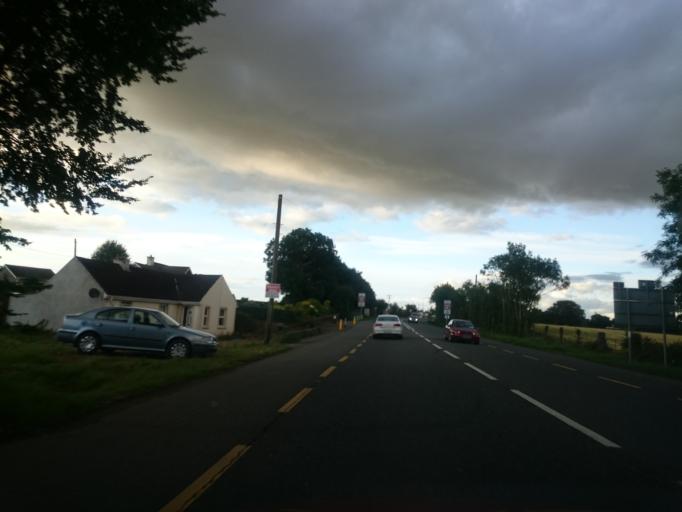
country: IE
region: Leinster
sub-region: Loch Garman
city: Ferns
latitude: 52.5860
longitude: -6.5068
